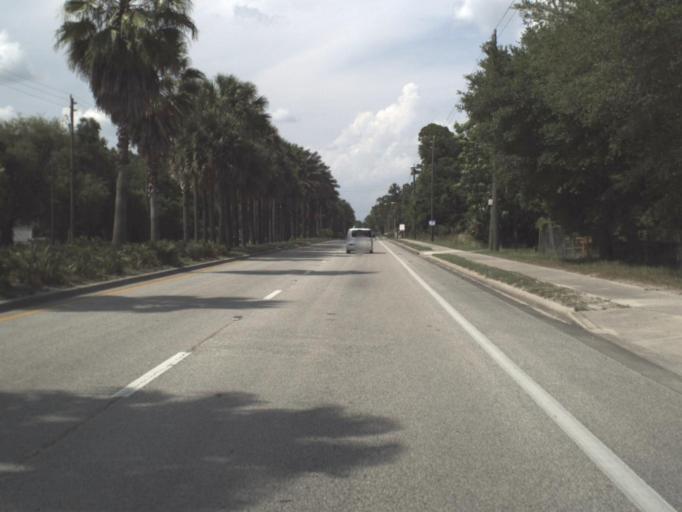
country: US
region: Florida
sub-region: Putnam County
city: East Palatka
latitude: 29.6528
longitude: -81.5947
